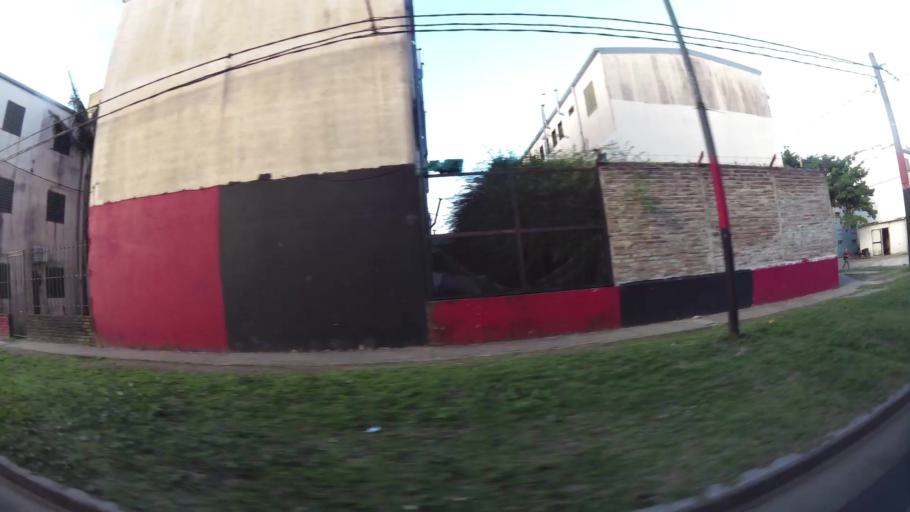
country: AR
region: Santa Fe
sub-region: Departamento de Rosario
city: Rosario
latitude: -32.9800
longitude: -60.6684
